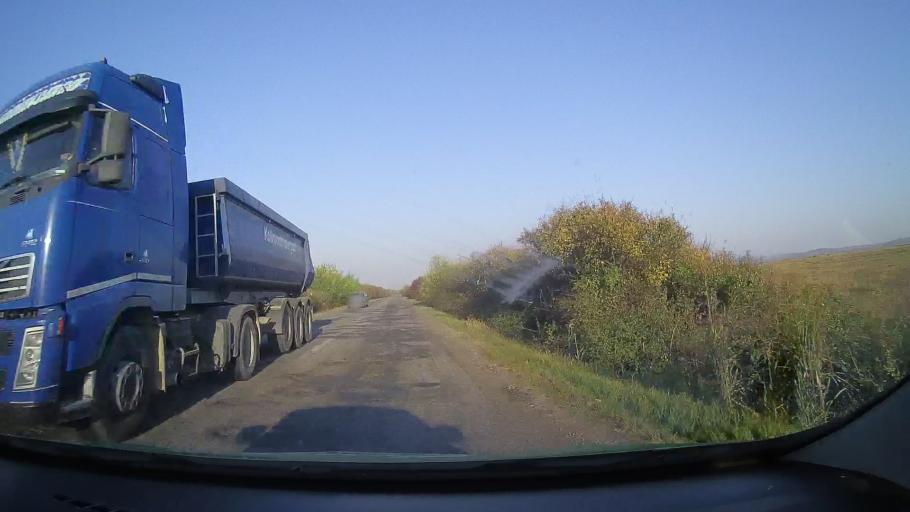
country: RO
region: Arad
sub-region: Comuna Tarnova
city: Agrisu Mare
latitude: 46.3121
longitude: 21.7537
